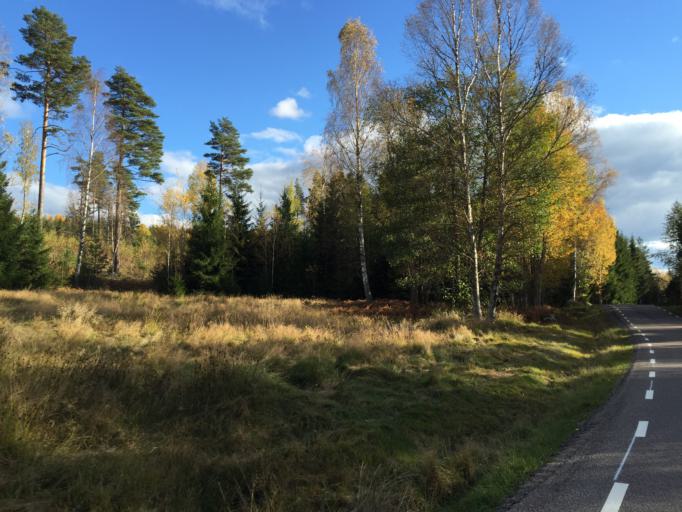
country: SE
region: Soedermanland
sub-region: Vingakers Kommun
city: Vingaker
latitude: 58.9641
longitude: 15.6555
